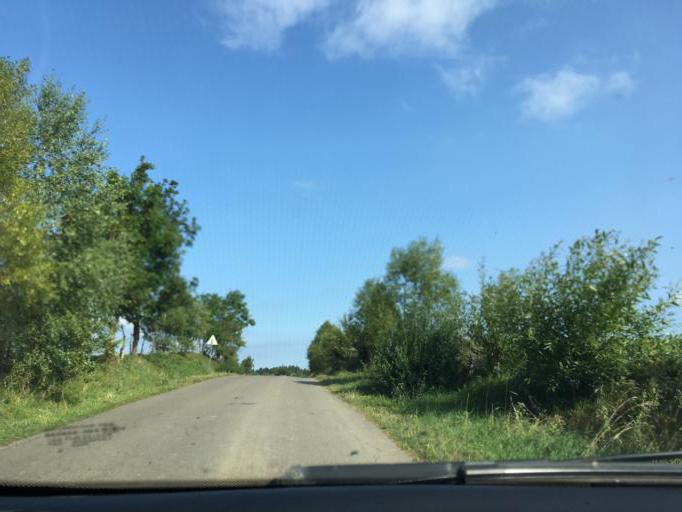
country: PL
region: Subcarpathian Voivodeship
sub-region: Powiat bieszczadzki
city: Lutowiska
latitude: 49.3023
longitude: 22.7038
